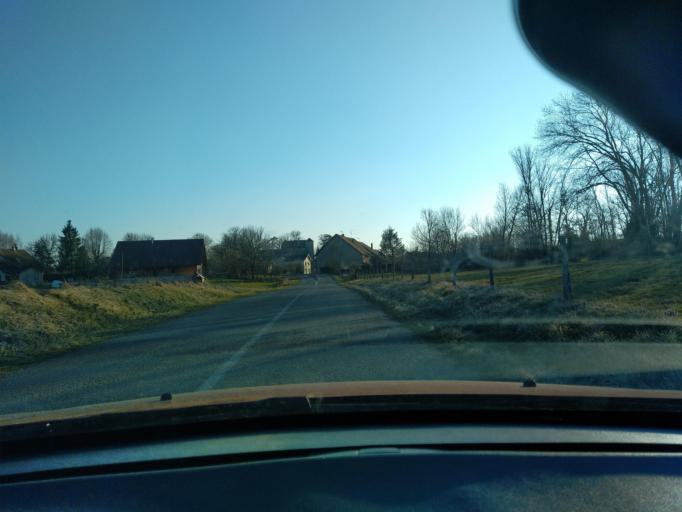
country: FR
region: Franche-Comte
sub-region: Departement du Jura
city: Perrigny
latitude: 46.6364
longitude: 5.6434
